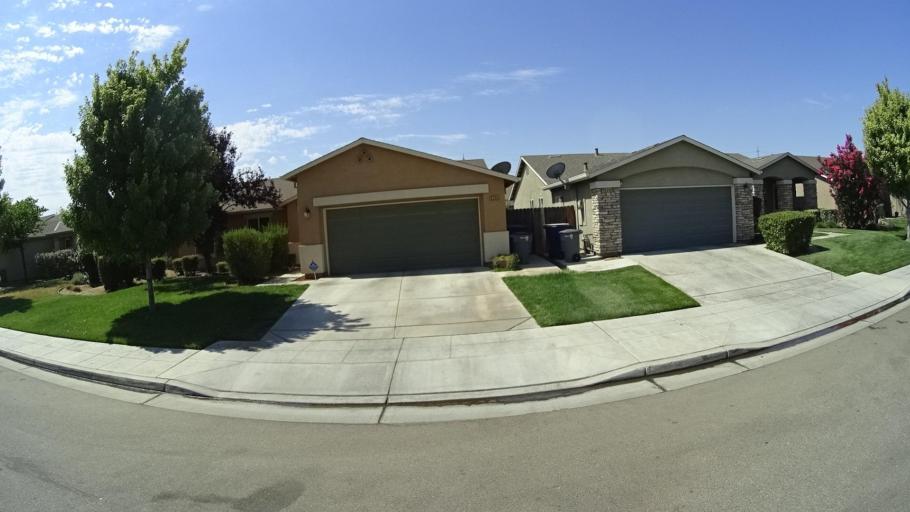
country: US
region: California
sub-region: Fresno County
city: Sunnyside
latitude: 36.7091
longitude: -119.7155
